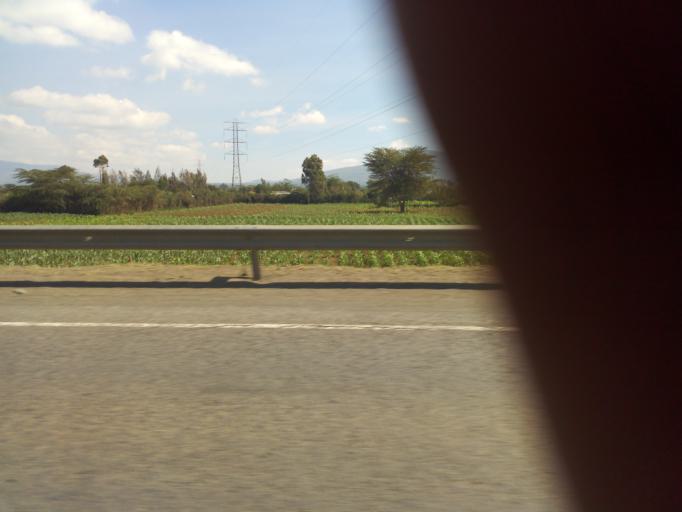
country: KE
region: Nakuru
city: Kijabe
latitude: -0.9897
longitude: 36.5729
